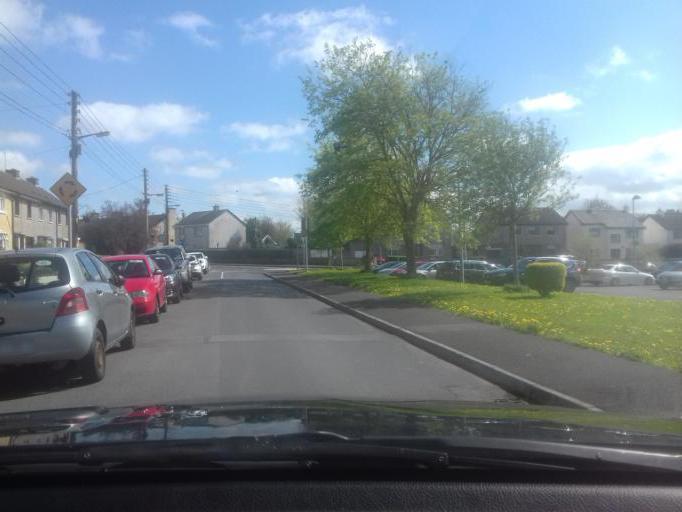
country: IE
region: Leinster
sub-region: Laois
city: Portlaoise
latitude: 53.0388
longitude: -7.2948
